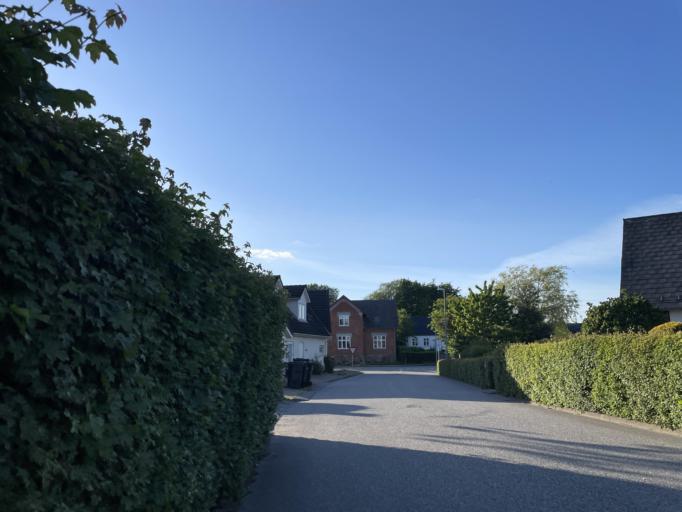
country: DK
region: South Denmark
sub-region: Vejle Kommune
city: Jelling
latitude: 55.7564
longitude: 9.4262
